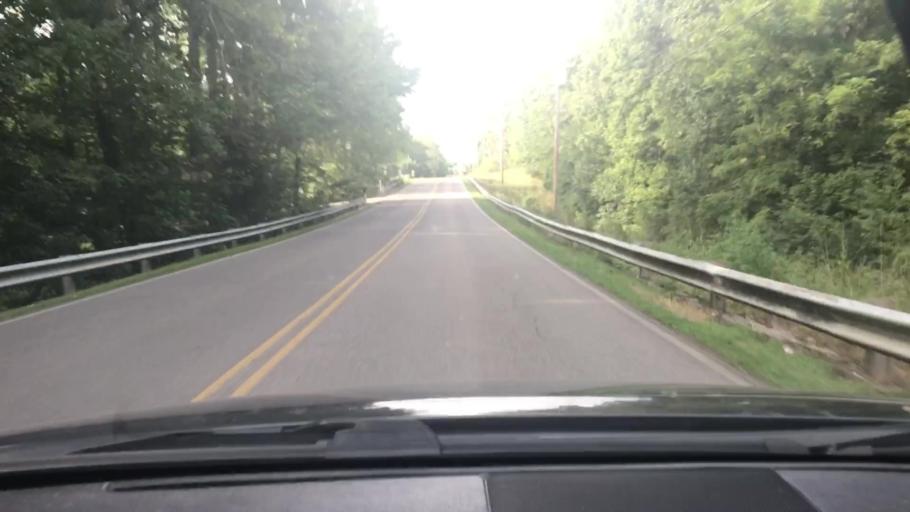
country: US
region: Tennessee
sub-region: Dickson County
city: White Bluff
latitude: 36.0986
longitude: -87.2142
